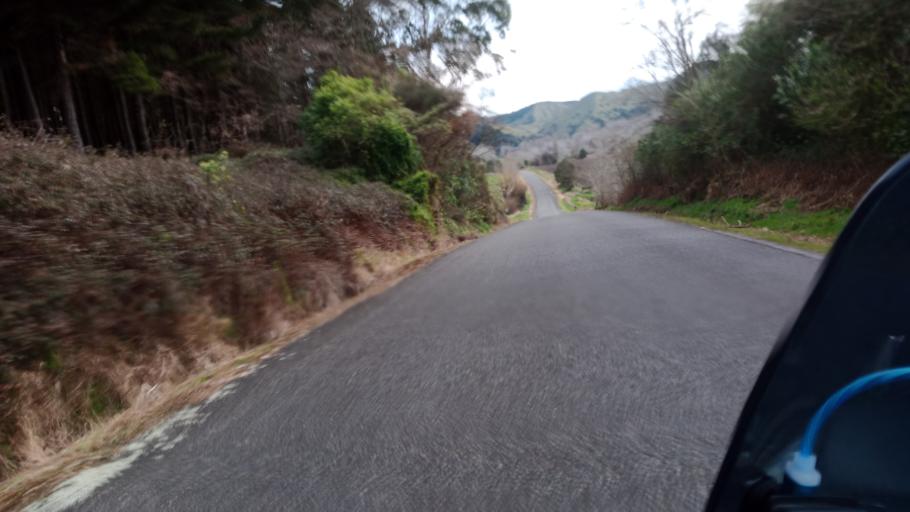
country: NZ
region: Hawke's Bay
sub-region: Wairoa District
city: Wairoa
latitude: -38.8211
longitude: 177.4932
